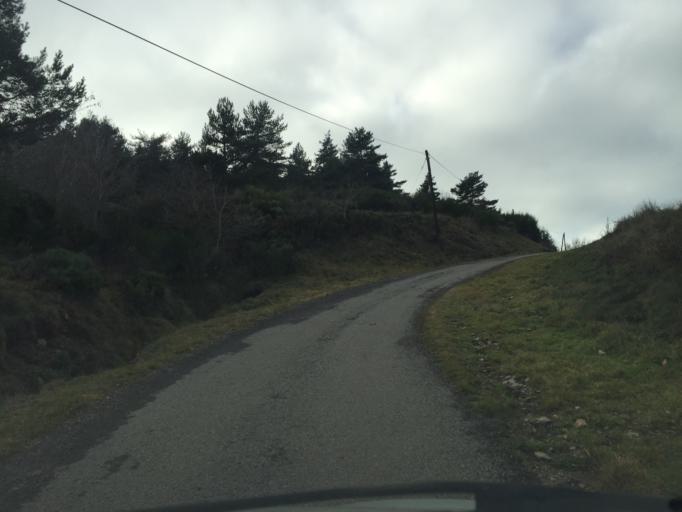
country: FR
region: Rhone-Alpes
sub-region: Departement de l'Ardeche
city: Les Vans
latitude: 44.5133
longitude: 3.9581
